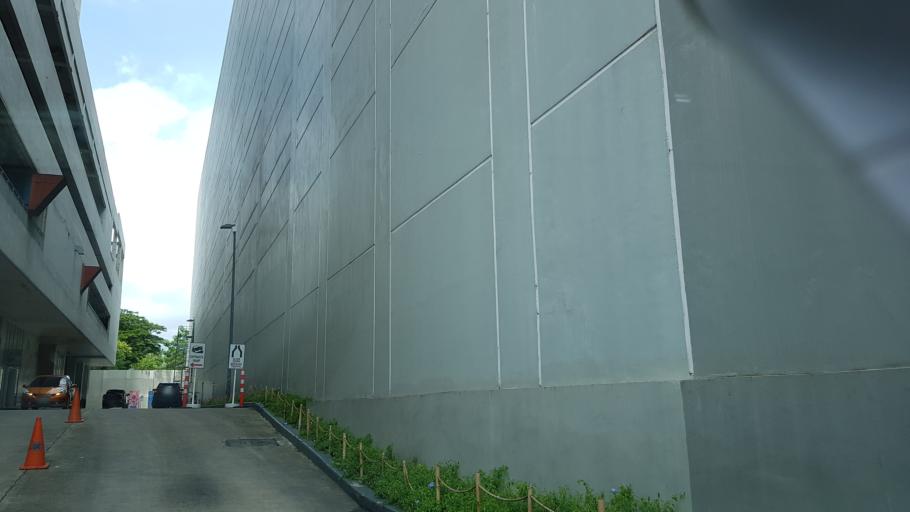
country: PH
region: Metro Manila
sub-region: Makati City
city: Makati City
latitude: 14.5641
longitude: 121.0225
